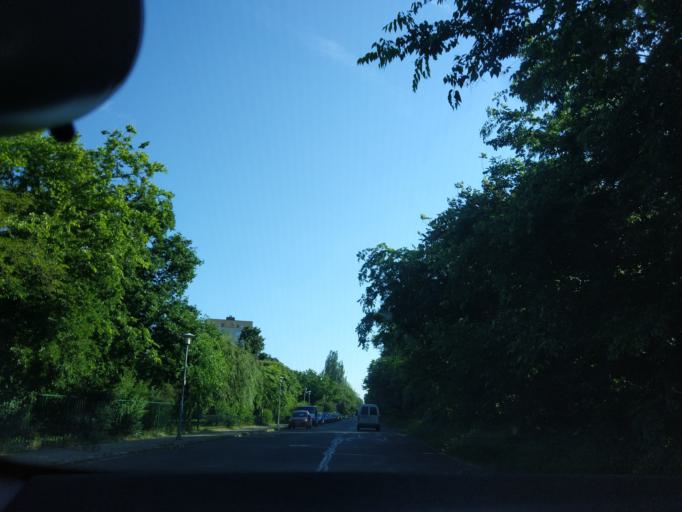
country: HU
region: Budapest
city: Budapest XIX. keruelet
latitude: 47.4633
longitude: 19.1198
